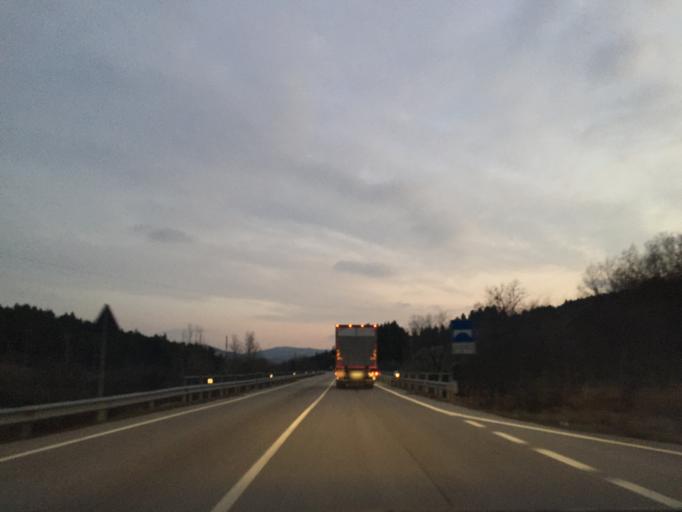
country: IT
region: Apulia
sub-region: Provincia di Foggia
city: Volturara Appula
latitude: 41.4782
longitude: 15.0538
